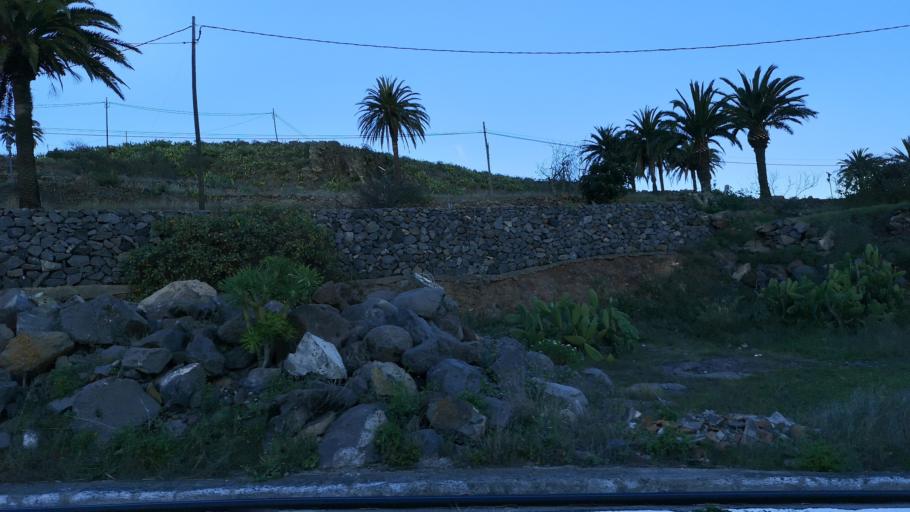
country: ES
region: Canary Islands
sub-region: Provincia de Santa Cruz de Tenerife
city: Alajero
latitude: 28.0589
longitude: -17.2348
